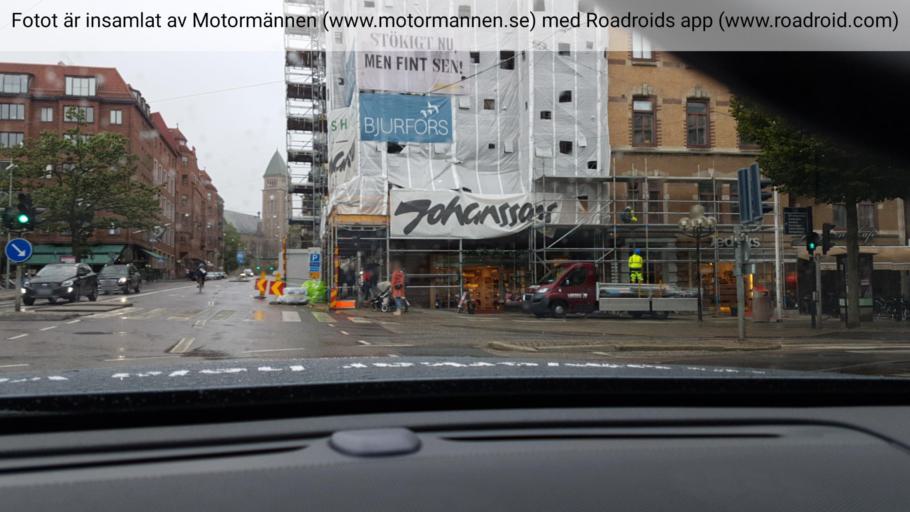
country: SE
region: Vaestra Goetaland
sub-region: Goteborg
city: Goeteborg
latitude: 57.6989
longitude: 11.9776
